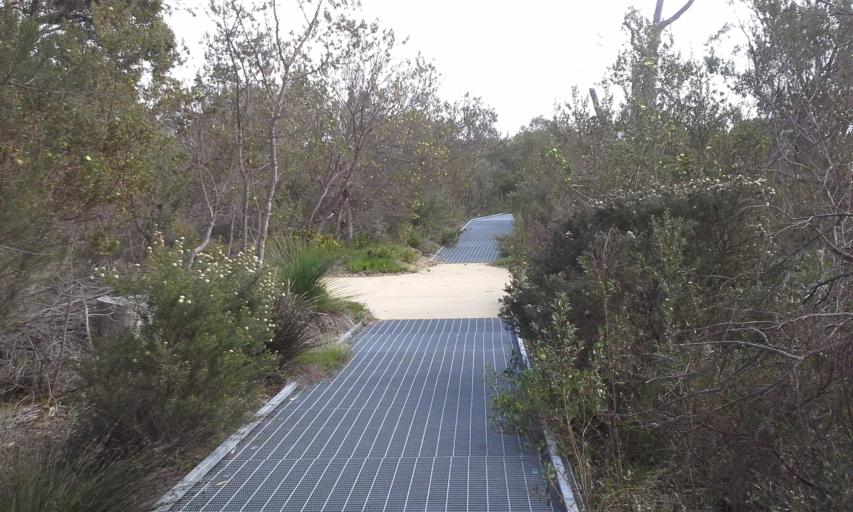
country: AU
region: Western Australia
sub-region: City of Perth
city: West Perth
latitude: -31.9628
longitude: 115.8366
